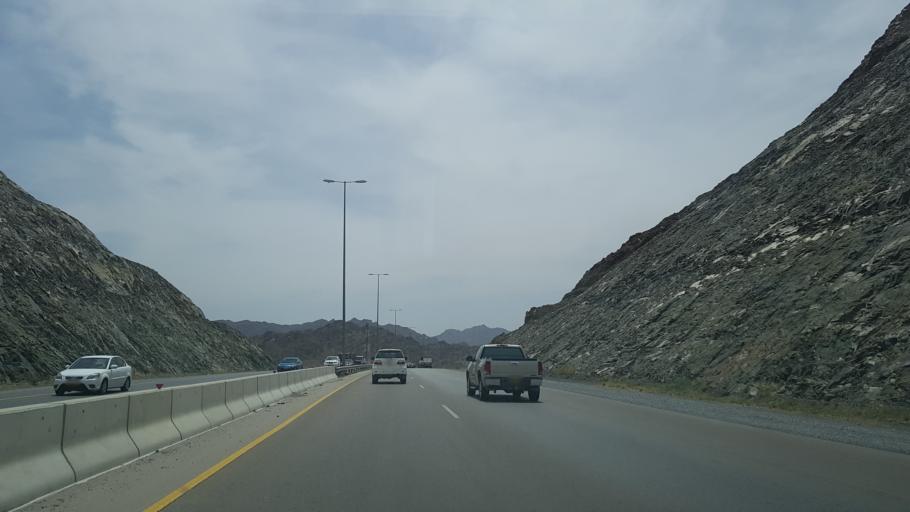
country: OM
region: Muhafazat ad Dakhiliyah
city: Izki
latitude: 22.9639
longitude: 57.7847
